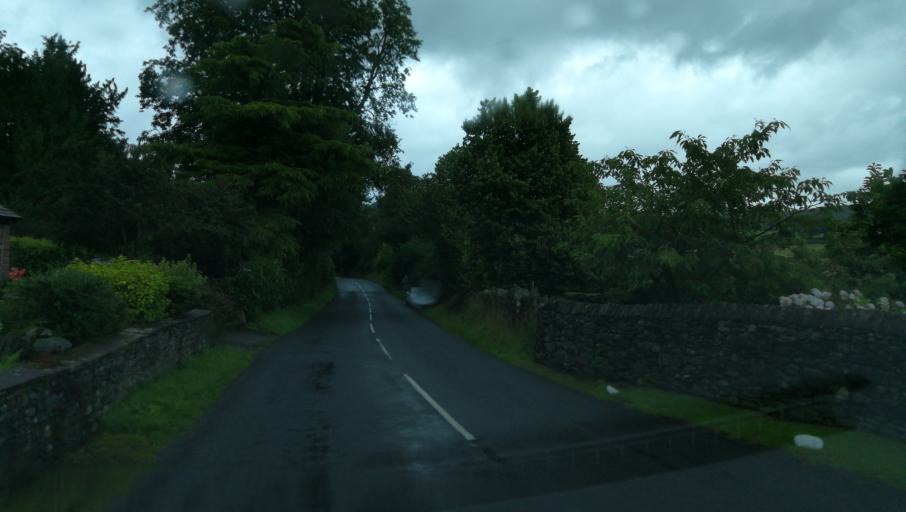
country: GB
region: England
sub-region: Cumbria
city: Penrith
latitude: 54.5945
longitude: -2.8587
